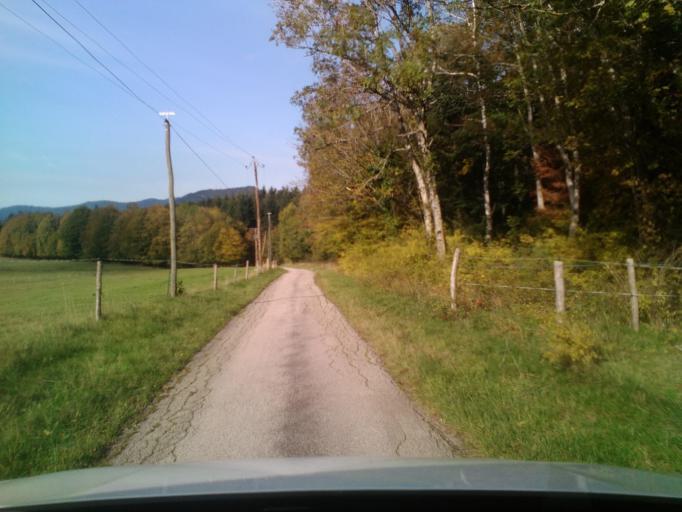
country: FR
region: Lorraine
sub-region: Departement des Vosges
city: Senones
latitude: 48.4042
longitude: 7.0749
